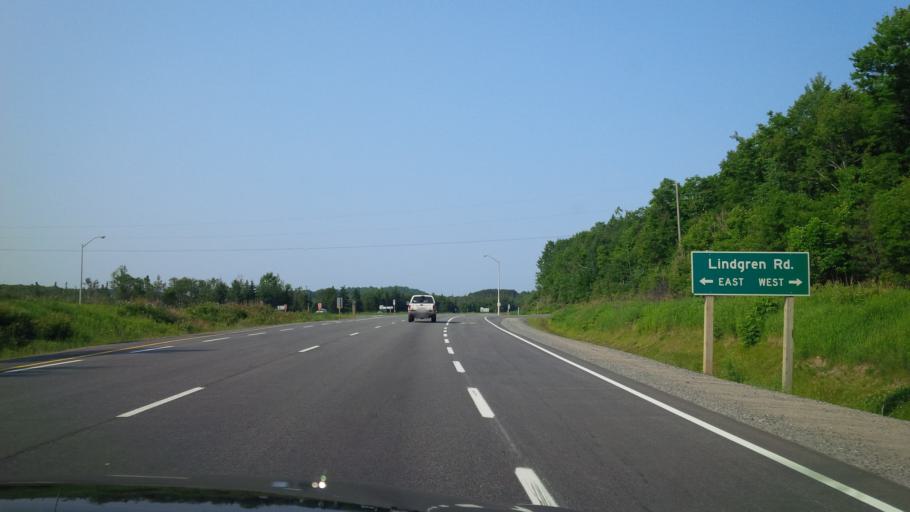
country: CA
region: Ontario
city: Huntsville
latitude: 45.3042
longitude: -79.2493
